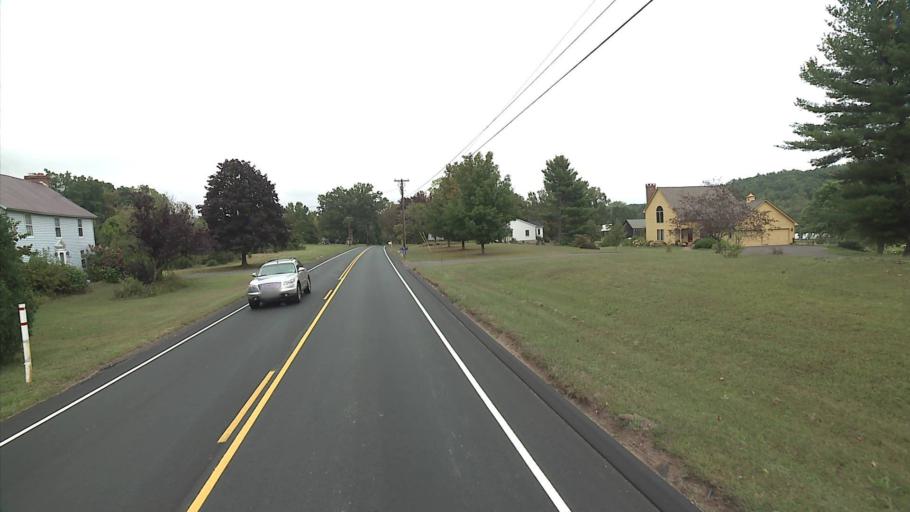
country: US
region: Connecticut
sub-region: Hartford County
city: Suffield Depot
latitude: 42.0306
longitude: -72.6883
